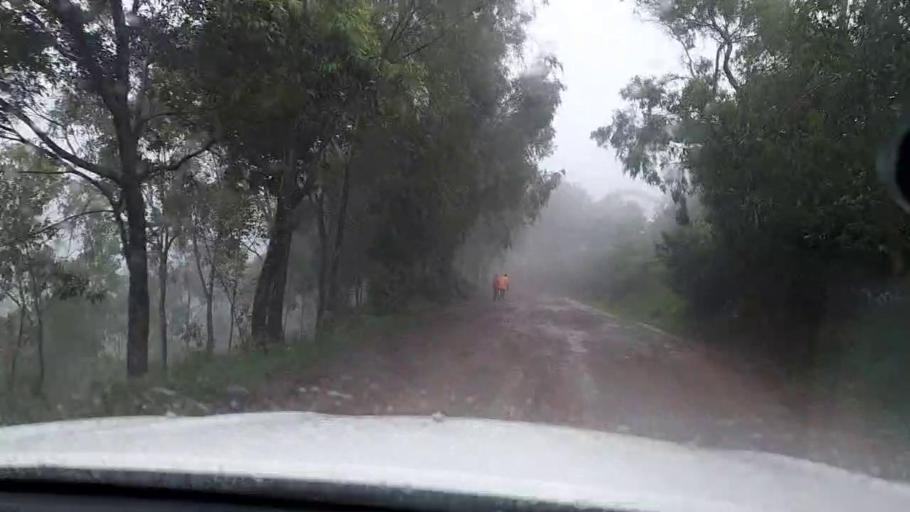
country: RW
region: Kigali
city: Kigali
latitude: -1.7736
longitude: 29.9994
